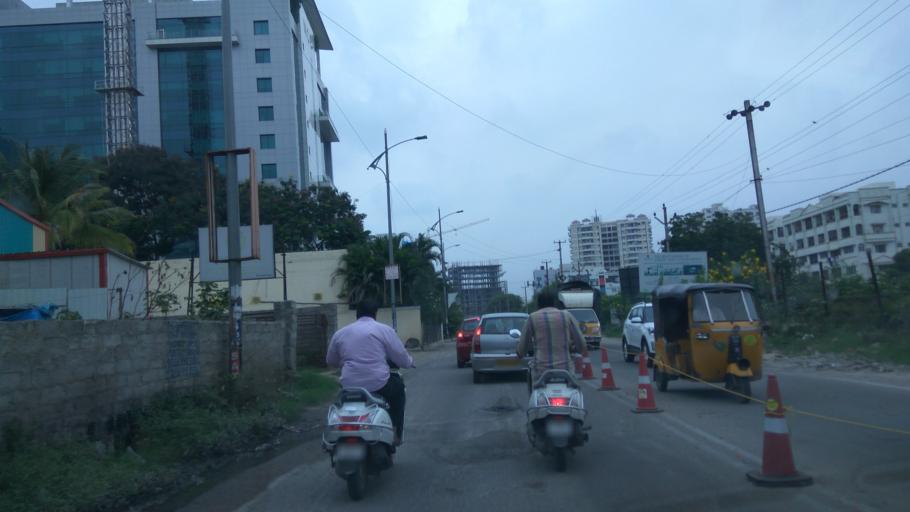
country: IN
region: Telangana
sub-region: Rangareddi
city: Kukatpalli
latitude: 17.4353
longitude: 78.3883
